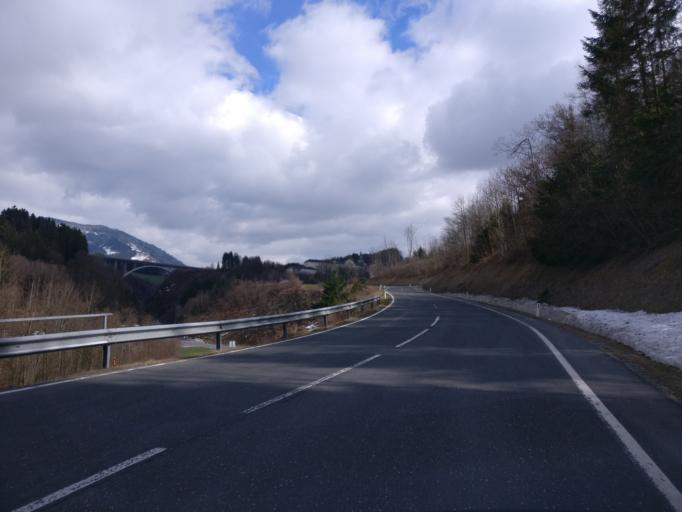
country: AT
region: Salzburg
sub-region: Politischer Bezirk Sankt Johann im Pongau
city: Bischofshofen
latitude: 47.4364
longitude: 13.2119
